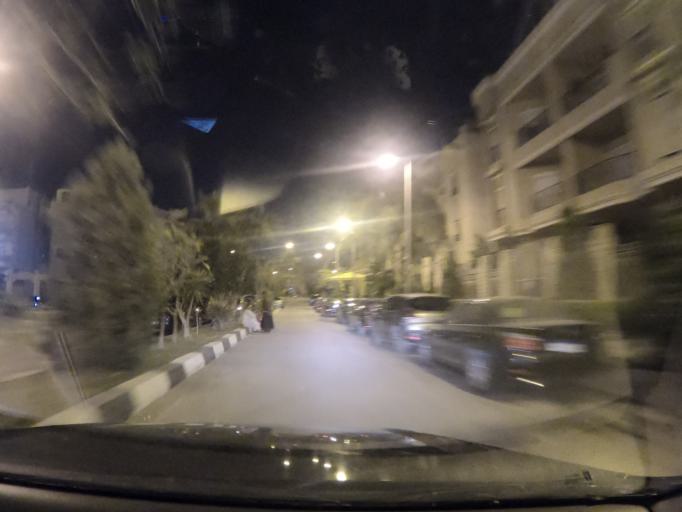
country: EG
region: Muhafazat al Qahirah
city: Cairo
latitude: 30.0148
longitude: 31.4263
